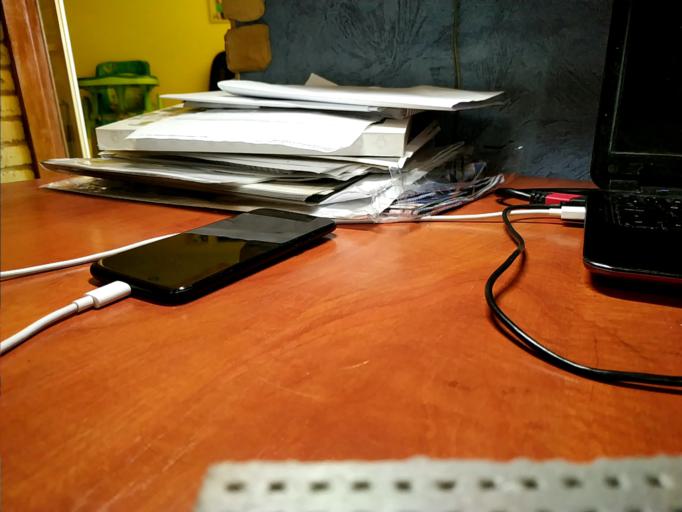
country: RU
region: Tverskaya
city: Kalashnikovo
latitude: 57.3975
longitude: 35.2486
